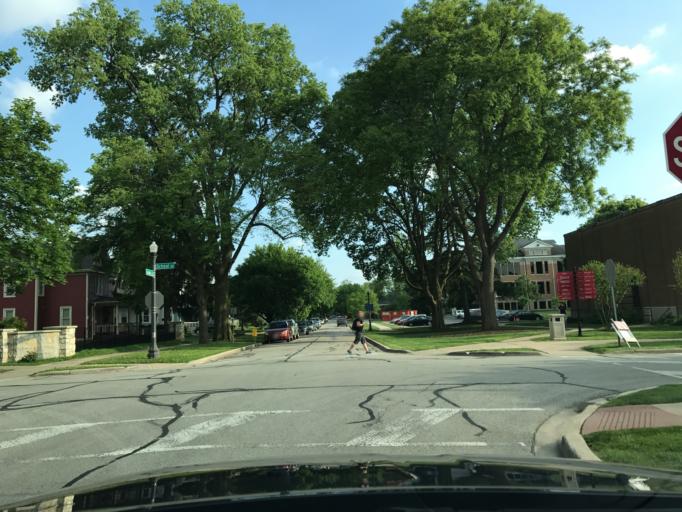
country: US
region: Illinois
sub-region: DuPage County
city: Naperville
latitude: 41.7778
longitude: -88.1421
